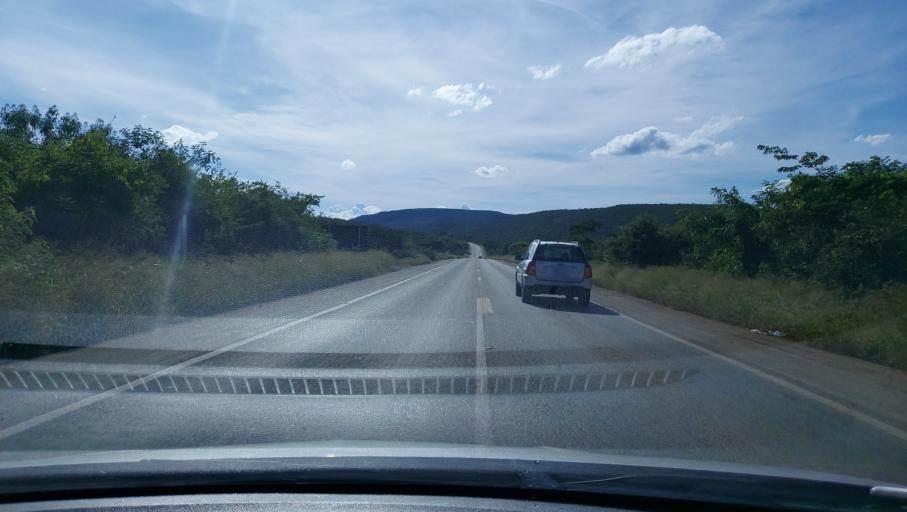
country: BR
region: Bahia
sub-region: Seabra
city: Seabra
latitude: -12.4574
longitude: -41.6499
